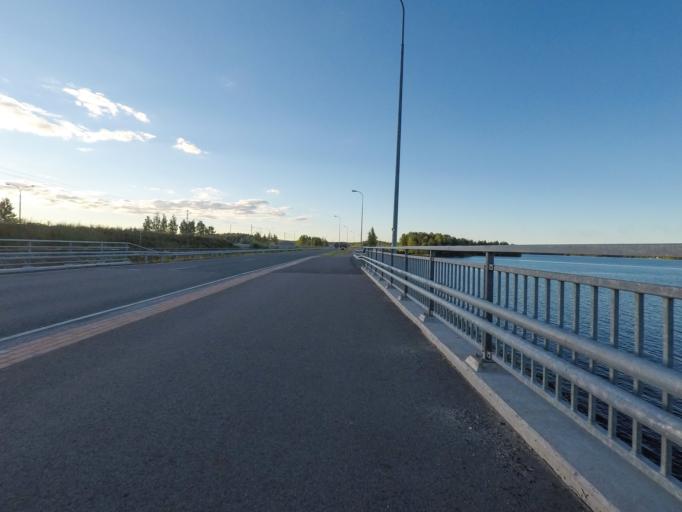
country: FI
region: Northern Savo
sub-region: Kuopio
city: Kuopio
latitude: 62.9379
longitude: 27.6678
